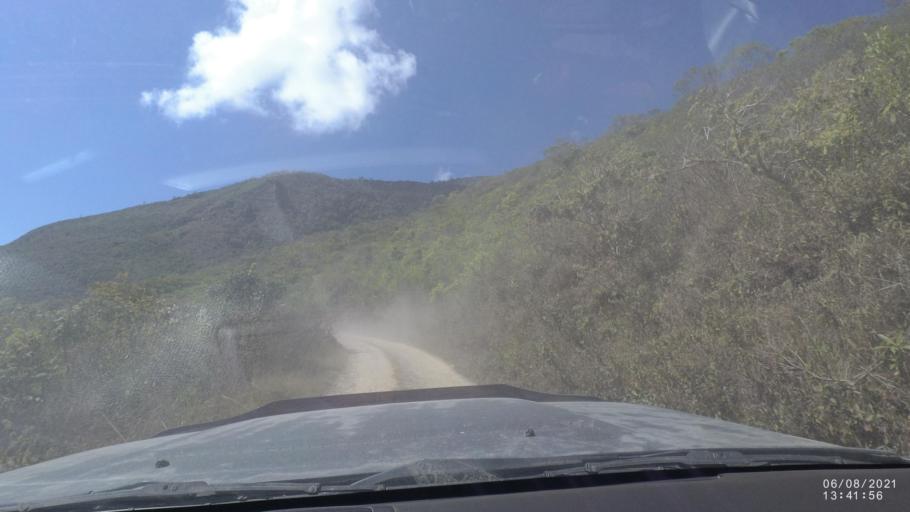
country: BO
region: La Paz
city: Quime
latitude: -16.6817
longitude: -66.7304
